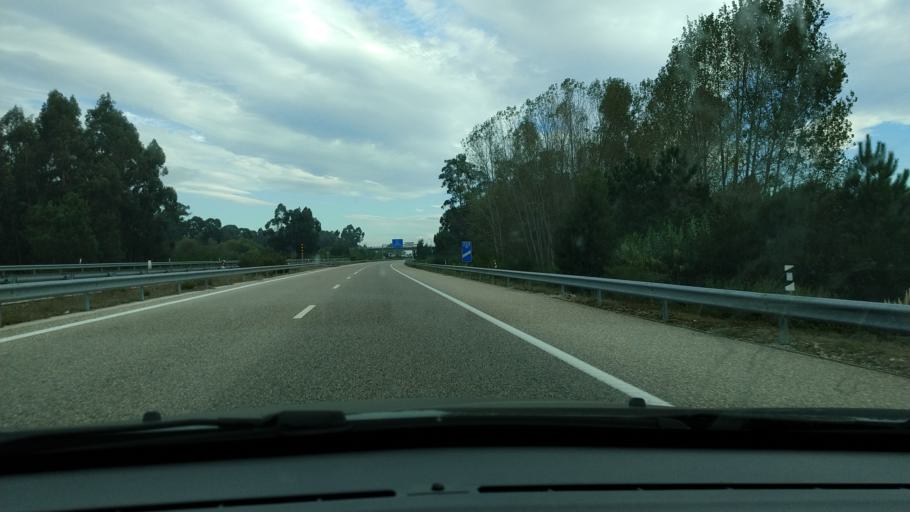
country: PT
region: Aveiro
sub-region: Vagos
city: Vagos
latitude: 40.4951
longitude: -8.6785
